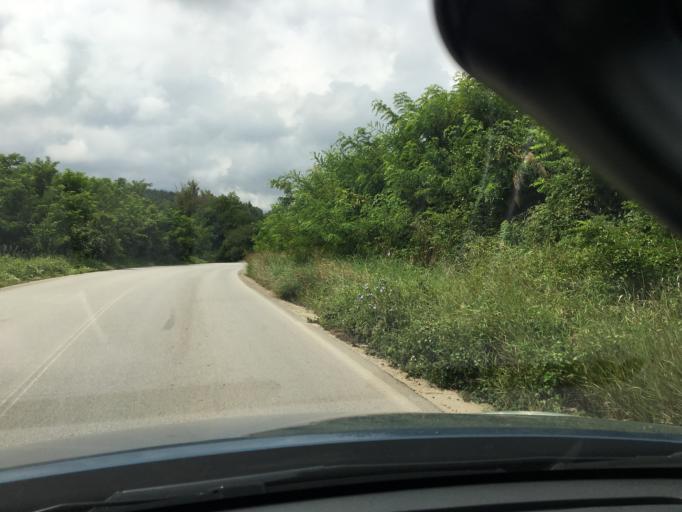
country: BG
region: Sofia-Capital
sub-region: Stolichna Obshtina
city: Sofia
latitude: 42.5980
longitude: 23.3680
